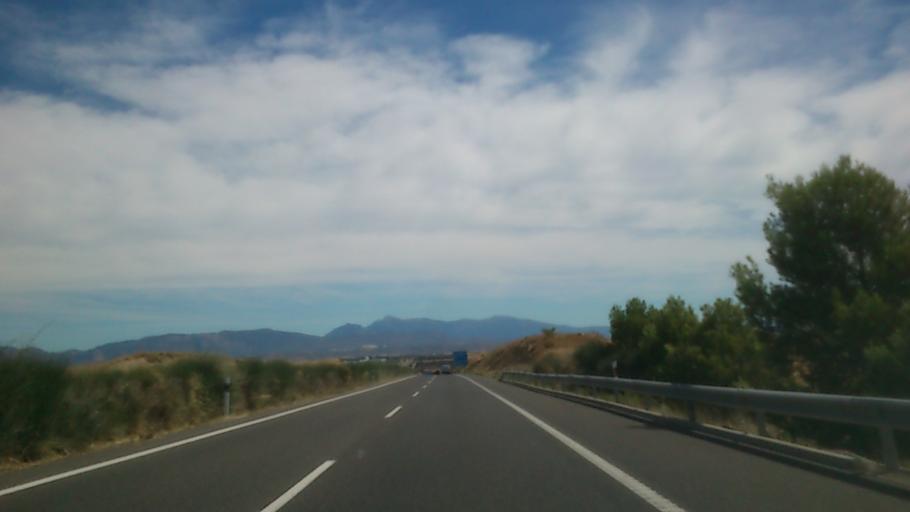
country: ES
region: Aragon
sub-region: Provincia de Huesca
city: Sangarren
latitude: 42.0791
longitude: -0.4923
